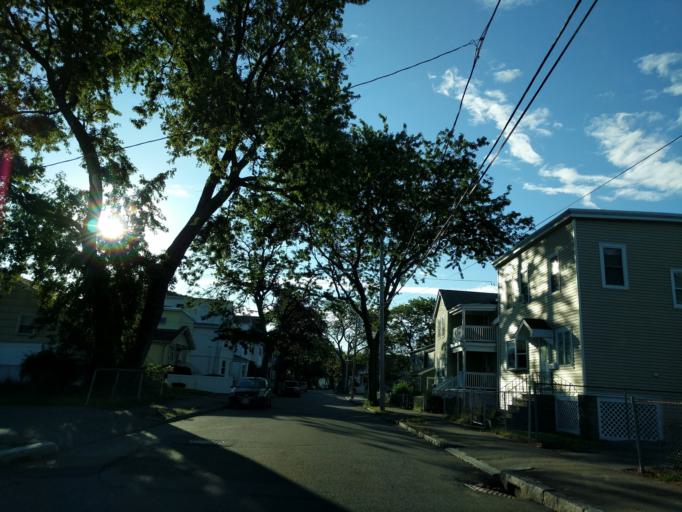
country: US
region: Massachusetts
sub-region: Middlesex County
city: Malden
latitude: 42.4271
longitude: -71.0526
